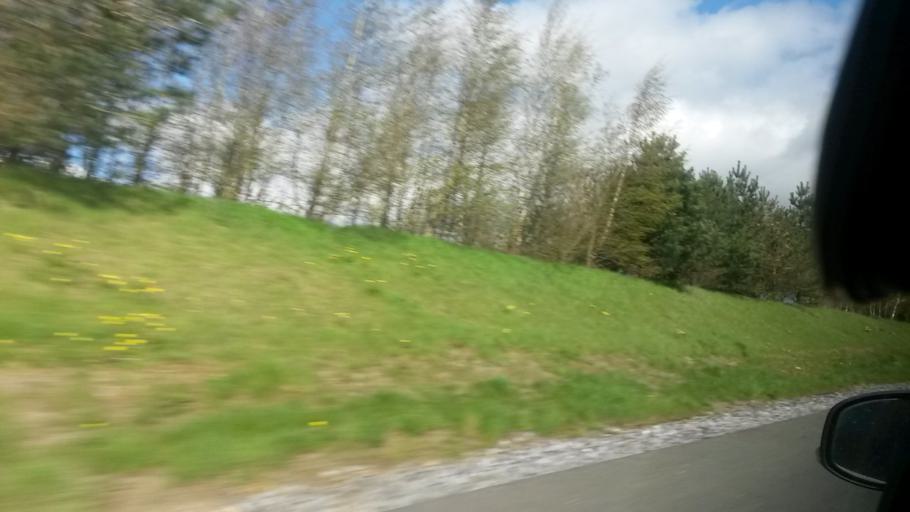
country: IE
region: Munster
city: Cahir
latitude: 52.4299
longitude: -7.9144
